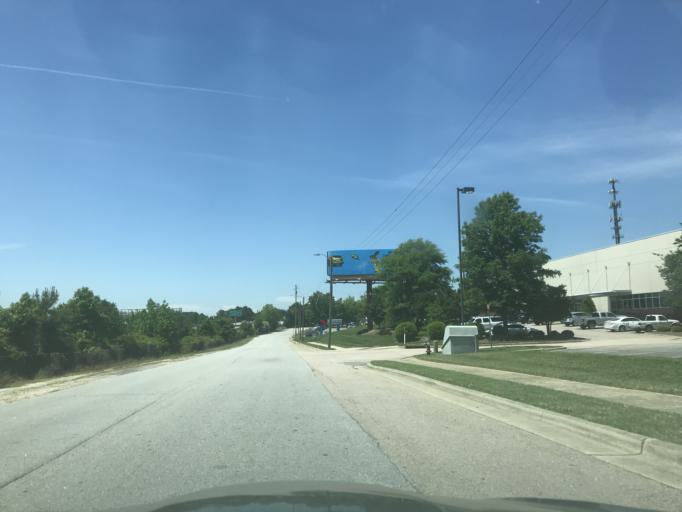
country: US
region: North Carolina
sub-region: Wake County
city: Raleigh
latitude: 35.8065
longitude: -78.5969
